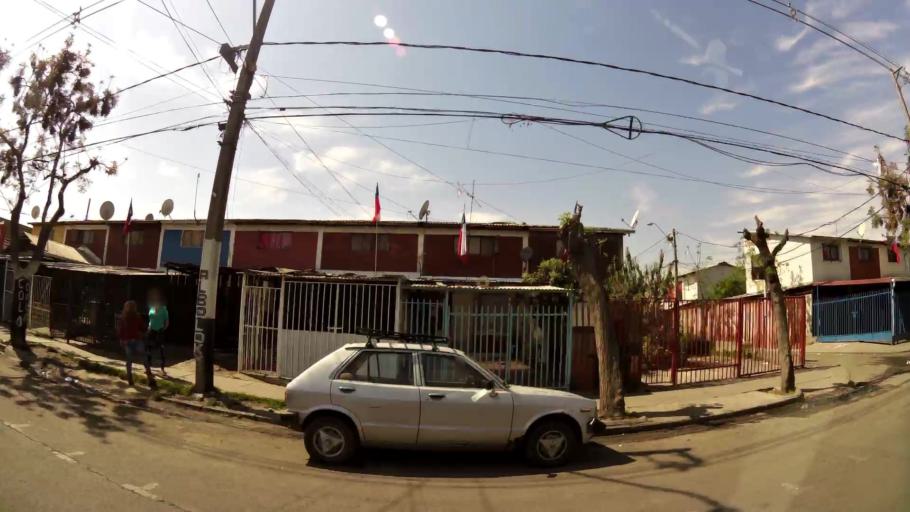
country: CL
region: Santiago Metropolitan
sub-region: Provincia de Santiago
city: La Pintana
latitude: -33.5624
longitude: -70.6384
